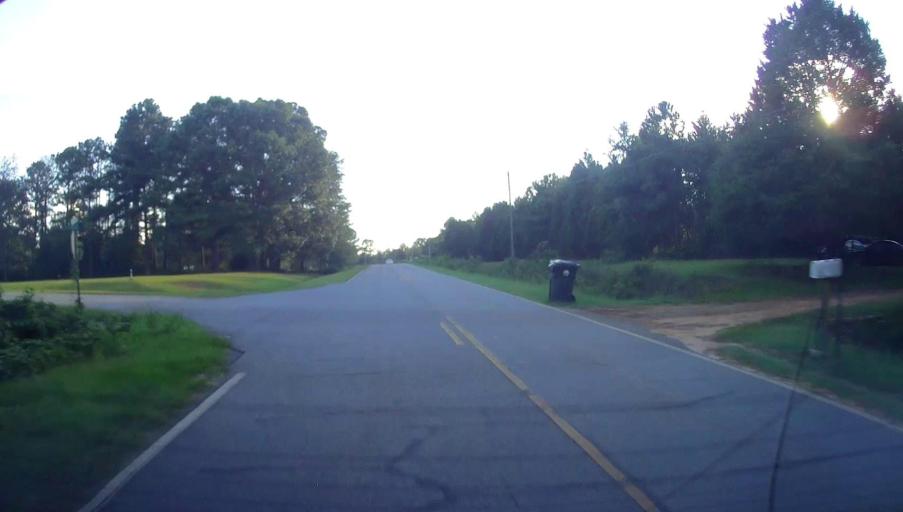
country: US
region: Georgia
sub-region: Peach County
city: Byron
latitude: 32.6227
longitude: -83.8245
